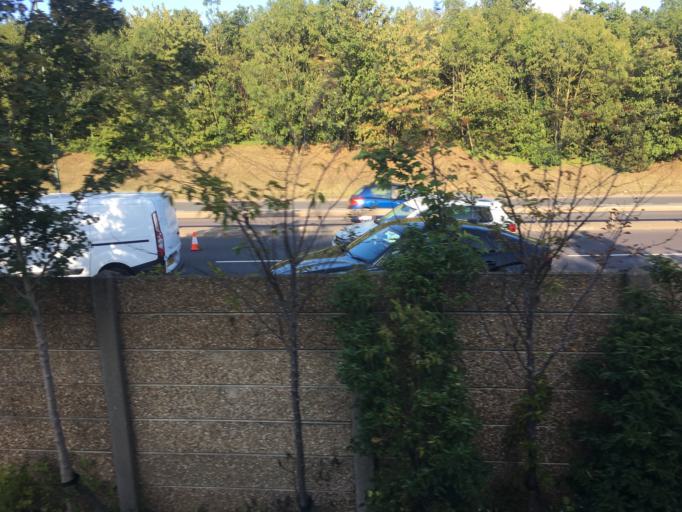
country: GB
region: England
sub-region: Greater London
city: Blackheath
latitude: 51.4718
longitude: 0.0261
